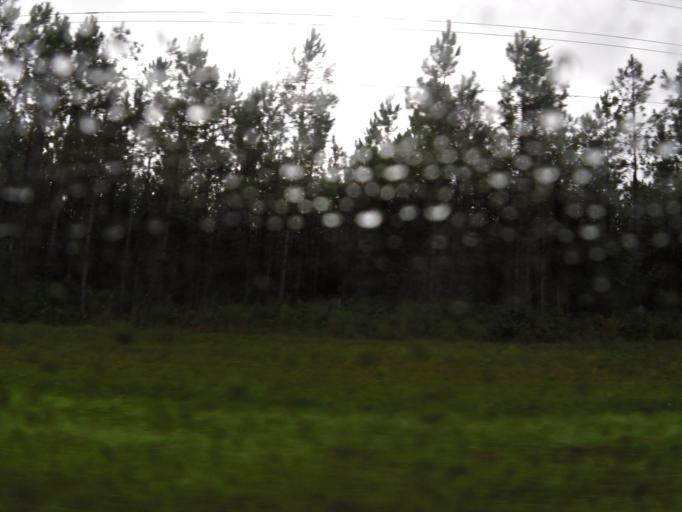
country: US
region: Florida
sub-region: Nassau County
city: Callahan
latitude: 30.5243
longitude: -81.9941
